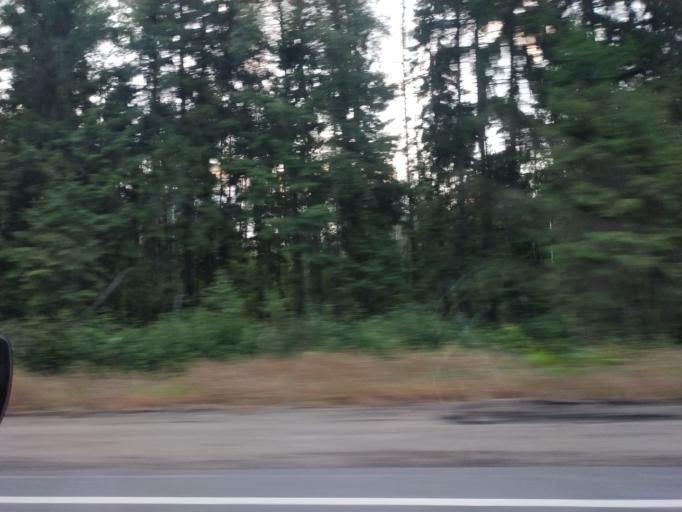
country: RU
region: Moskovskaya
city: Krasnoarmeysk
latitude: 56.0448
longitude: 38.2066
